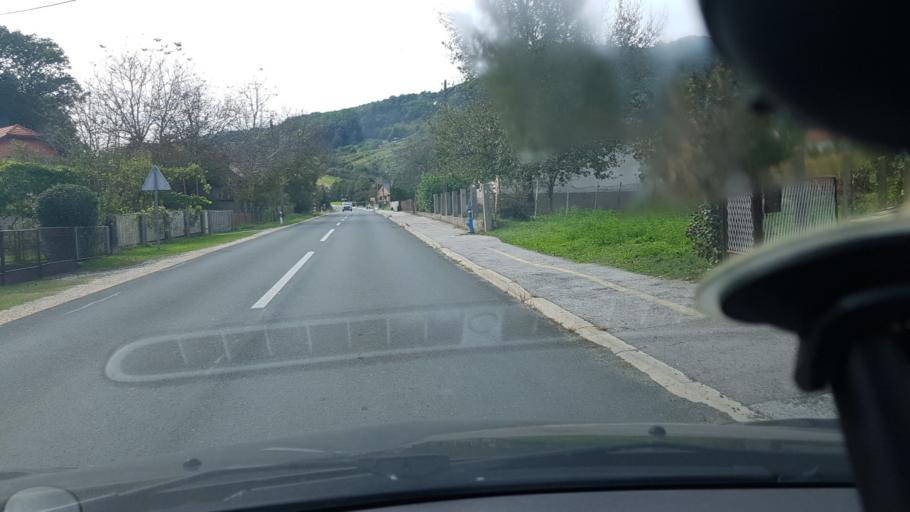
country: HR
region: Varazdinska
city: Remetinec
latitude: 46.1674
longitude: 16.3082
